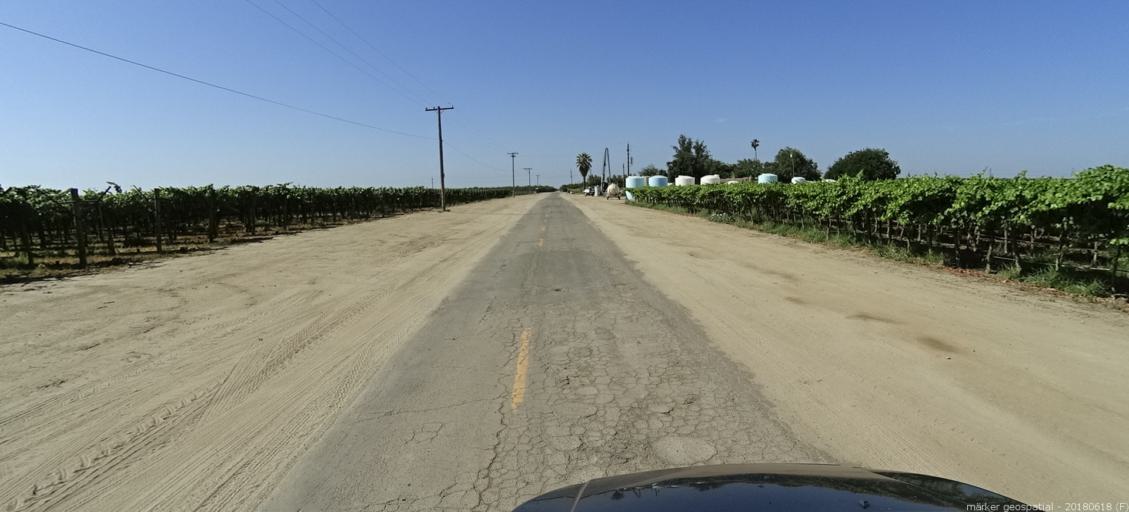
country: US
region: California
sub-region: Madera County
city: Parkwood
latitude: 36.8838
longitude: -120.1557
